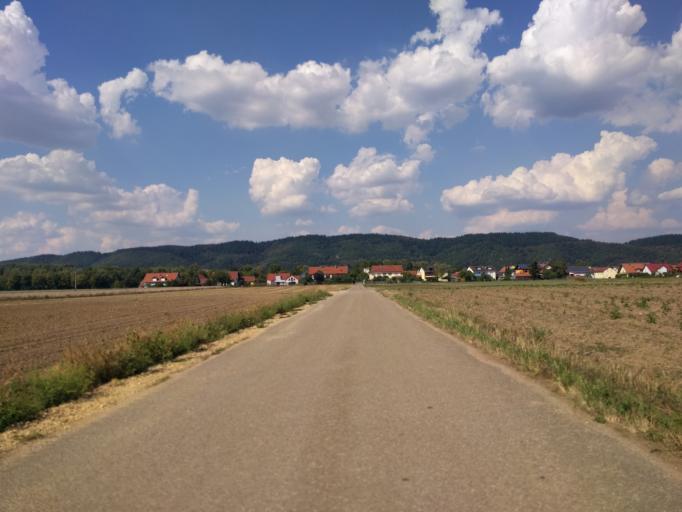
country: DE
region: Bavaria
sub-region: Upper Palatinate
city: Mintraching
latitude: 49.0043
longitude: 12.2715
